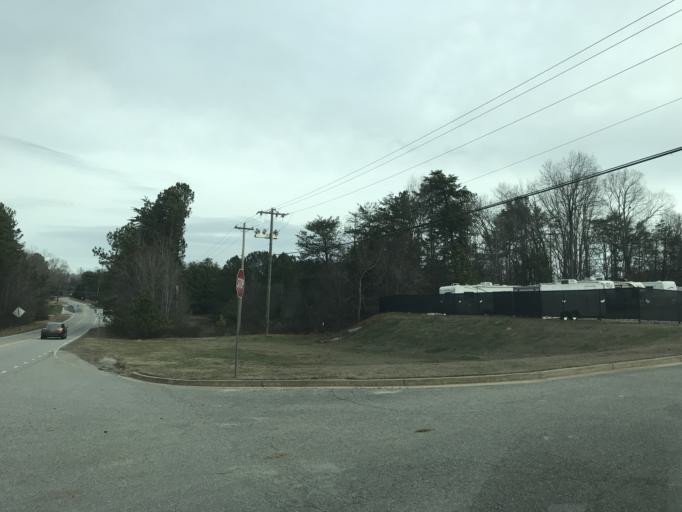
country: US
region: Georgia
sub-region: Forsyth County
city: Cumming
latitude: 34.2306
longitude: -84.1043
